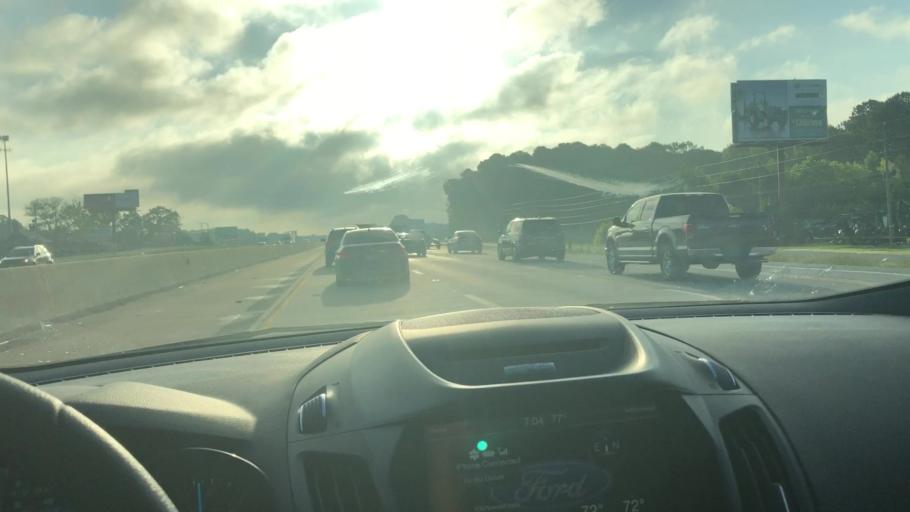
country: US
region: Arkansas
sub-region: Pulaski County
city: Alexander
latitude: 34.6343
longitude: -92.4609
